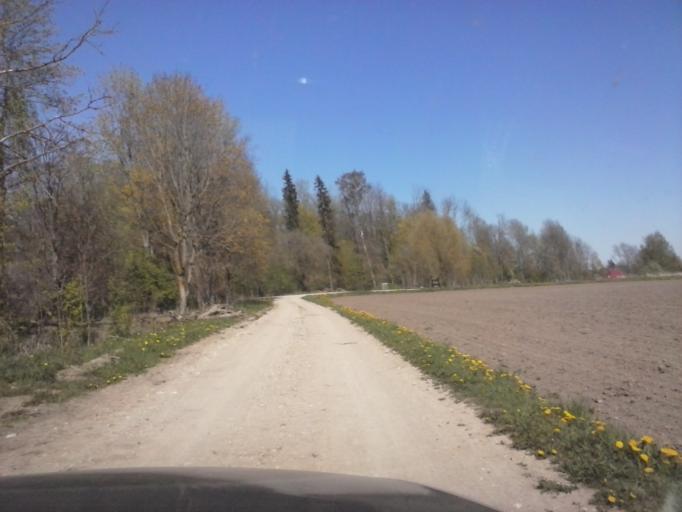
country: EE
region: Valgamaa
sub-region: Torva linn
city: Torva
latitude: 58.2328
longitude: 25.9004
